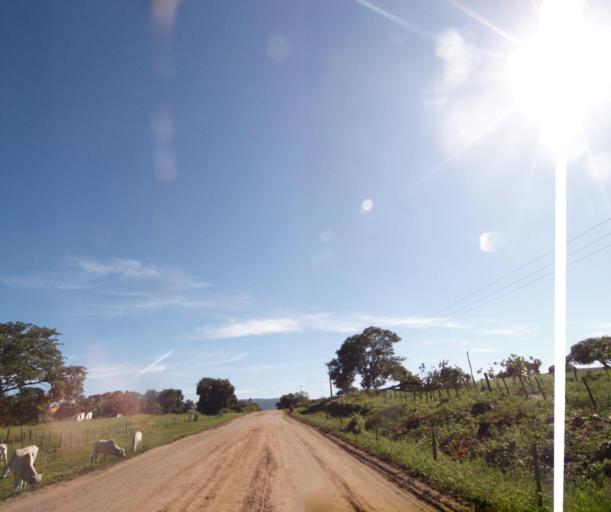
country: BR
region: Bahia
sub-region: Sao Felix Do Coribe
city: Santa Maria da Vitoria
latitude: -13.6269
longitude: -44.4222
